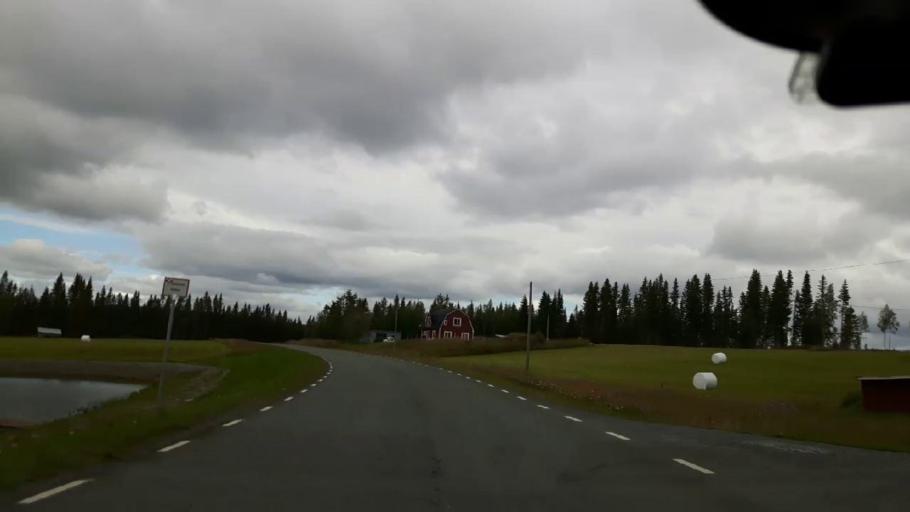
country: SE
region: Jaemtland
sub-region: Krokoms Kommun
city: Valla
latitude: 63.5426
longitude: 13.8560
